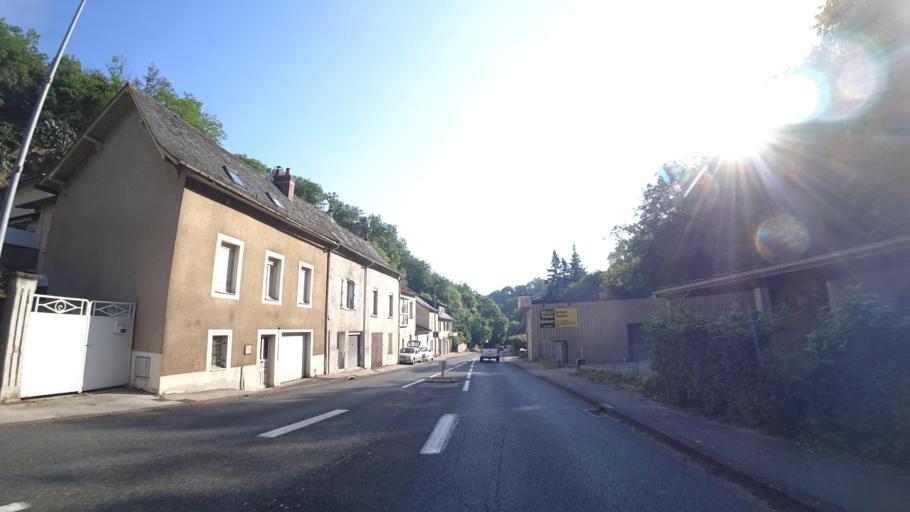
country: FR
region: Midi-Pyrenees
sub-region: Departement de l'Aveyron
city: Olemps
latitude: 44.3372
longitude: 2.5618
